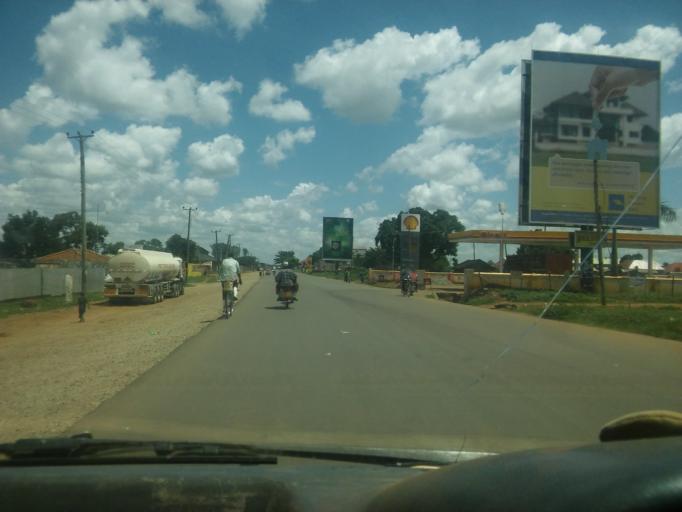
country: UG
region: Eastern Region
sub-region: Mbale District
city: Mbale
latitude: 1.0796
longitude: 34.1540
